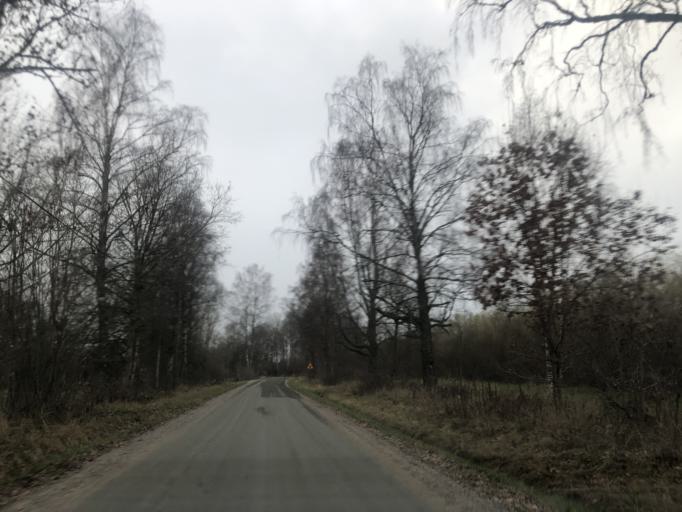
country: SE
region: Vaestra Goetaland
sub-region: Tranemo Kommun
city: Limmared
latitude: 57.6563
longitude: 13.3579
